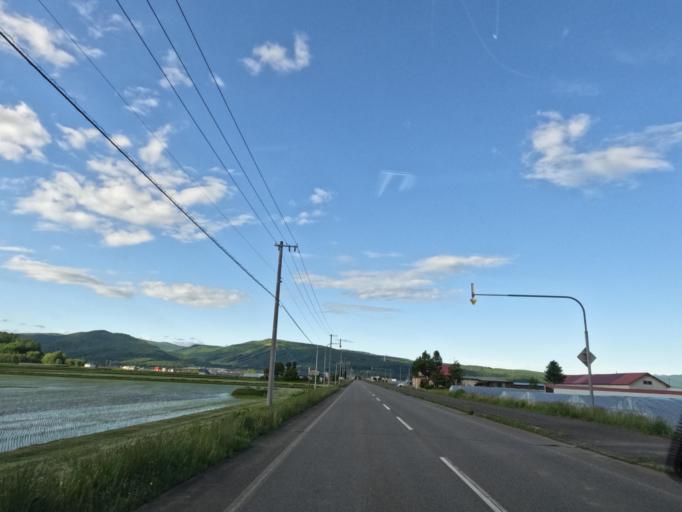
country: JP
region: Hokkaido
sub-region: Asahikawa-shi
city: Asahikawa
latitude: 43.8937
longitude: 142.4702
